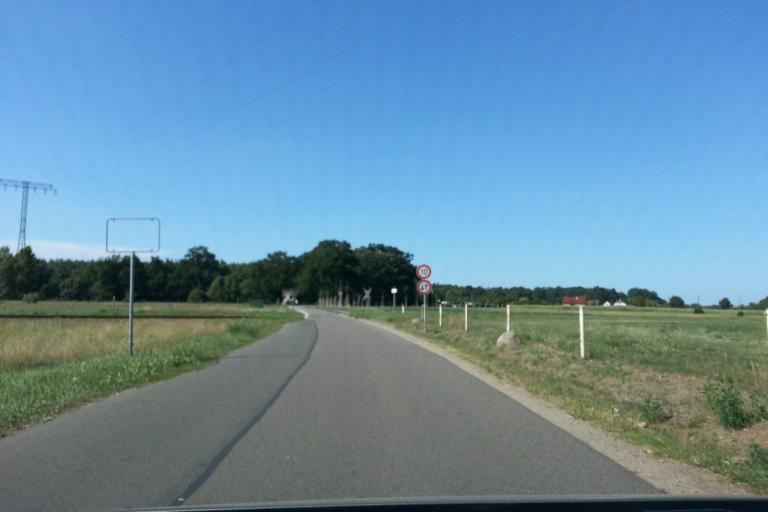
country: DE
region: Mecklenburg-Vorpommern
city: Torgelow
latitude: 53.6409
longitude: 14.0262
